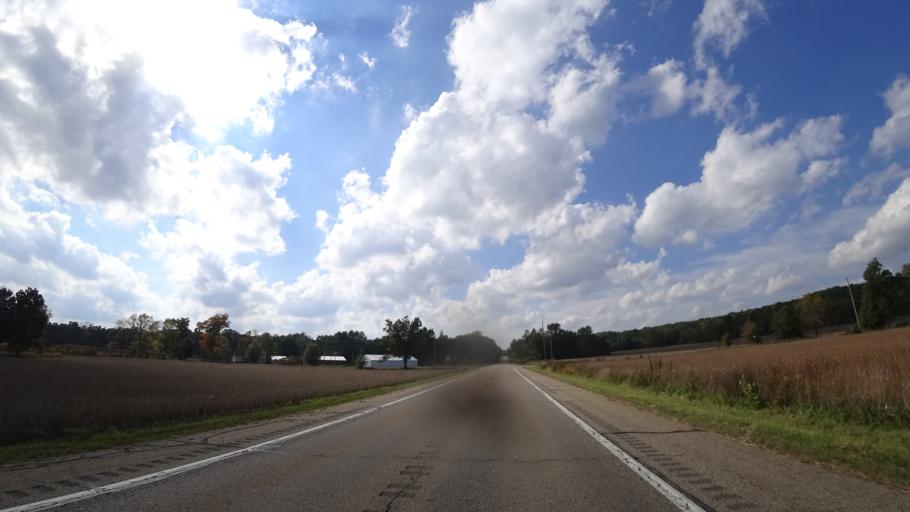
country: US
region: Michigan
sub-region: Branch County
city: Union City
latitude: 42.1054
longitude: -85.0314
